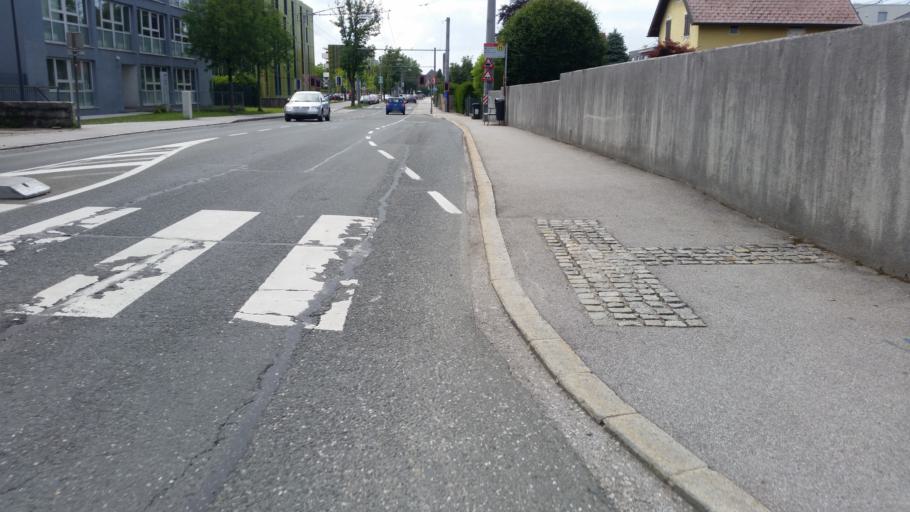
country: AT
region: Salzburg
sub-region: Politischer Bezirk Salzburg-Umgebung
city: Bergheim
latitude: 47.8089
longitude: 13.0143
